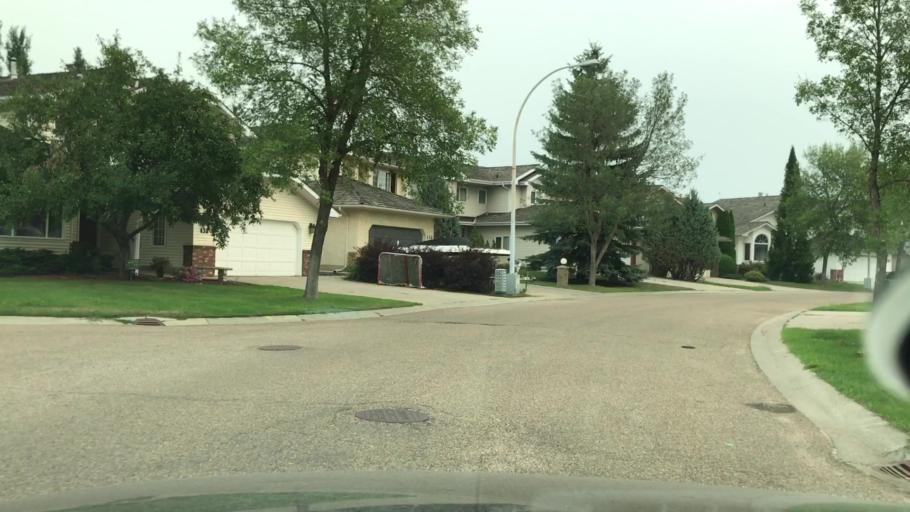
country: CA
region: Alberta
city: Edmonton
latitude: 53.4715
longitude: -113.5762
